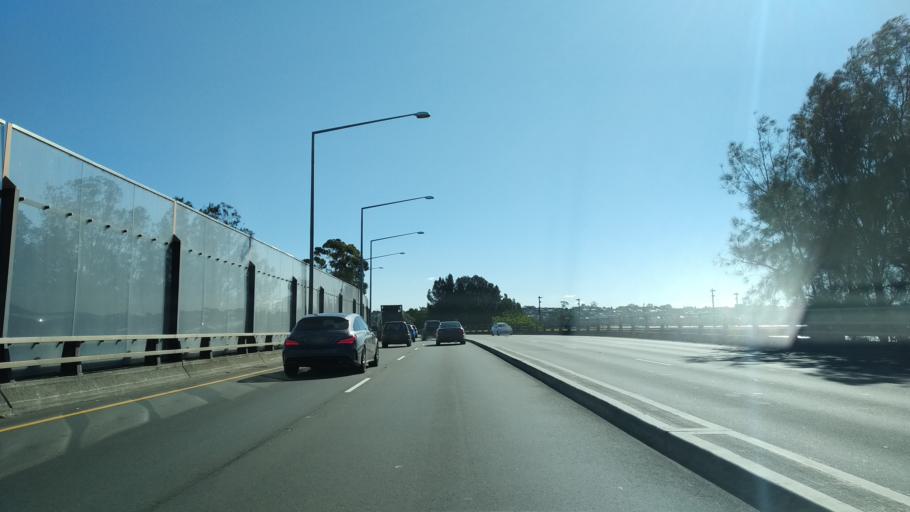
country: AU
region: New South Wales
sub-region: Leichhardt
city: Leichhardt
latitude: -33.8732
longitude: 151.1503
